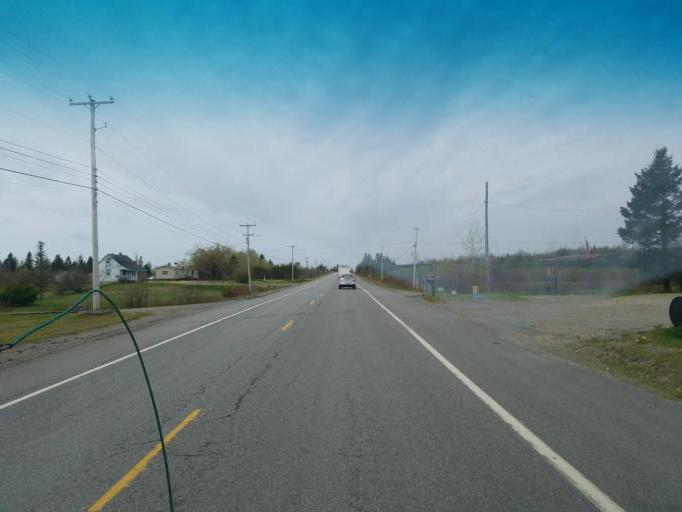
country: US
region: Maine
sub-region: Washington County
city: East Machias
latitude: 44.7568
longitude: -67.2302
